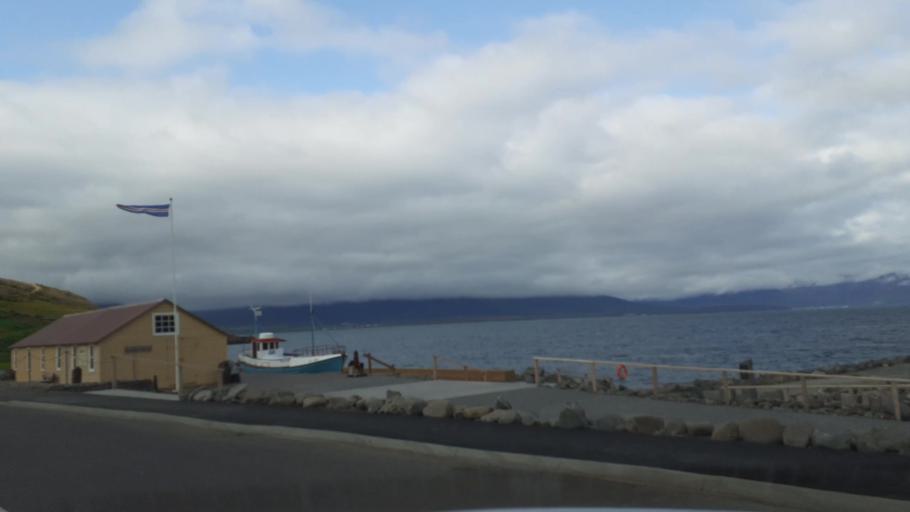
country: IS
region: Northeast
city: Akureyri
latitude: 65.9467
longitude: -18.1852
